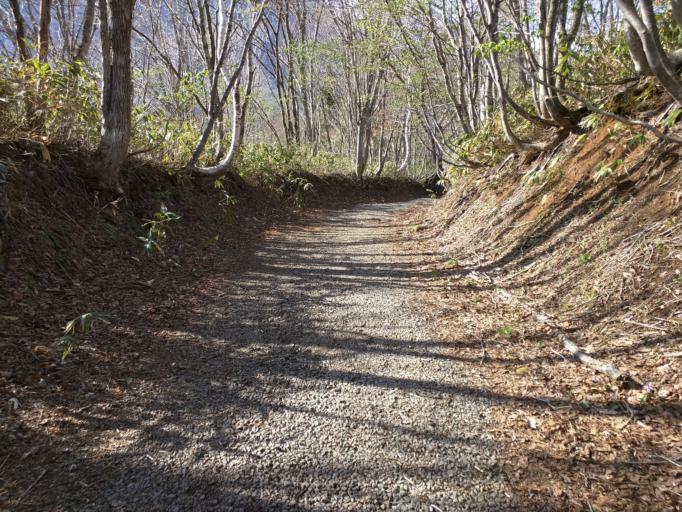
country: JP
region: Nagano
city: Nagano-shi
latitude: 36.7533
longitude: 138.0795
